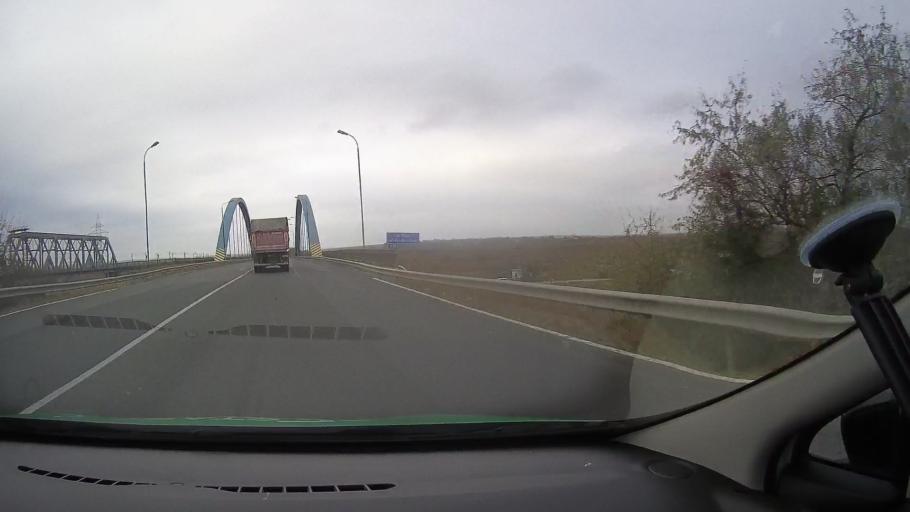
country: RO
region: Constanta
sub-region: Comuna Poarta Alba
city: Poarta Alba
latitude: 44.2164
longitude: 28.3896
